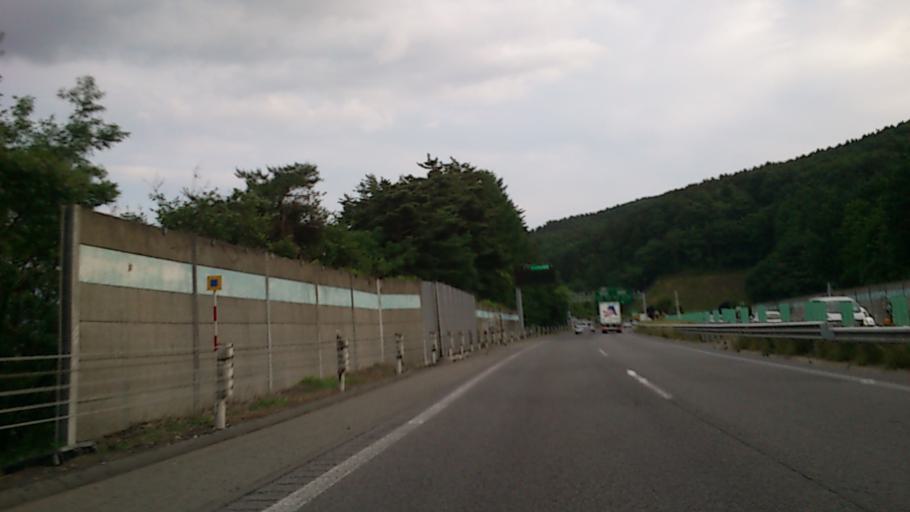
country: JP
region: Nagano
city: Okaya
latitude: 36.0759
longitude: 138.0389
